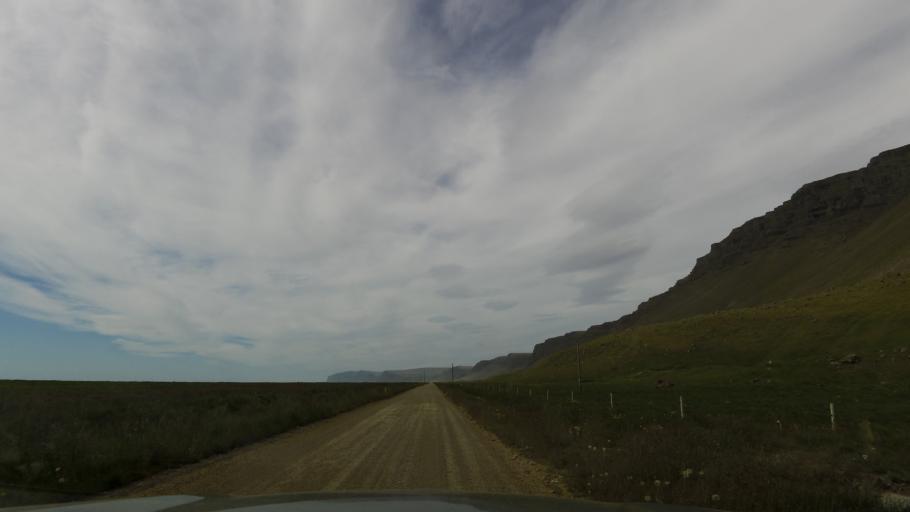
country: IS
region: West
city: Olafsvik
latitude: 65.4813
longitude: -24.0213
